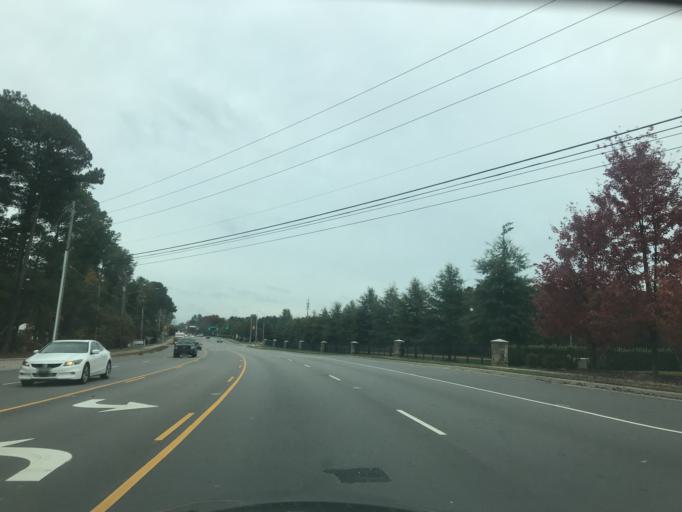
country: US
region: North Carolina
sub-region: Wake County
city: West Raleigh
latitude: 35.8872
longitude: -78.6276
